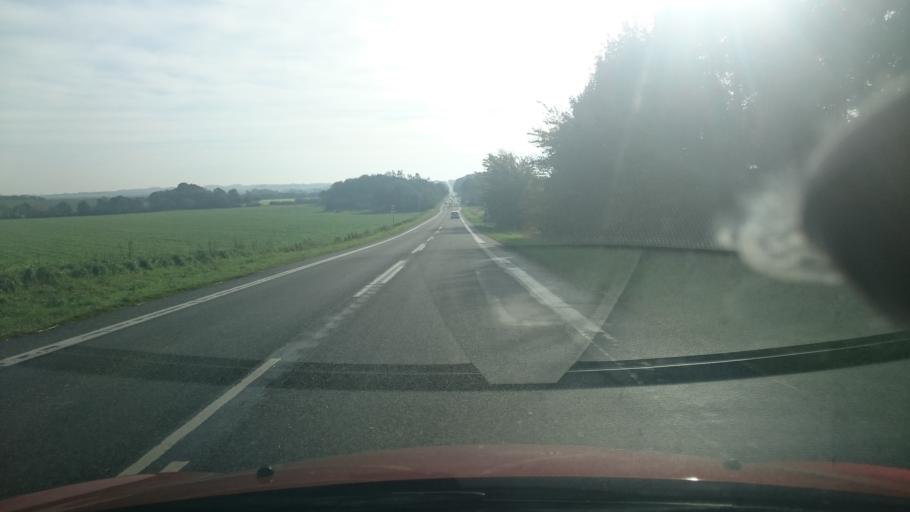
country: DK
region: Central Jutland
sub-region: Randers Kommune
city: Assentoft
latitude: 56.4103
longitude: 10.2277
